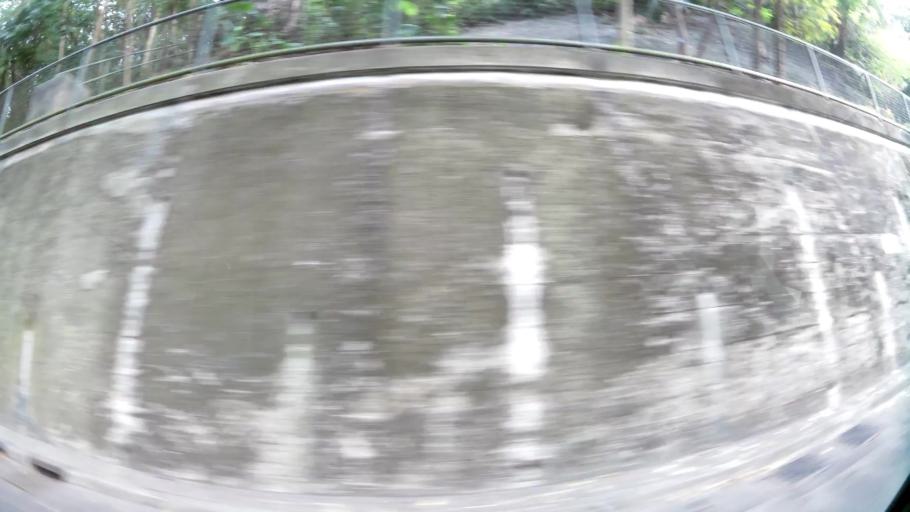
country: HK
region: Central and Western
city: Central
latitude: 22.2770
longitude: 114.1624
